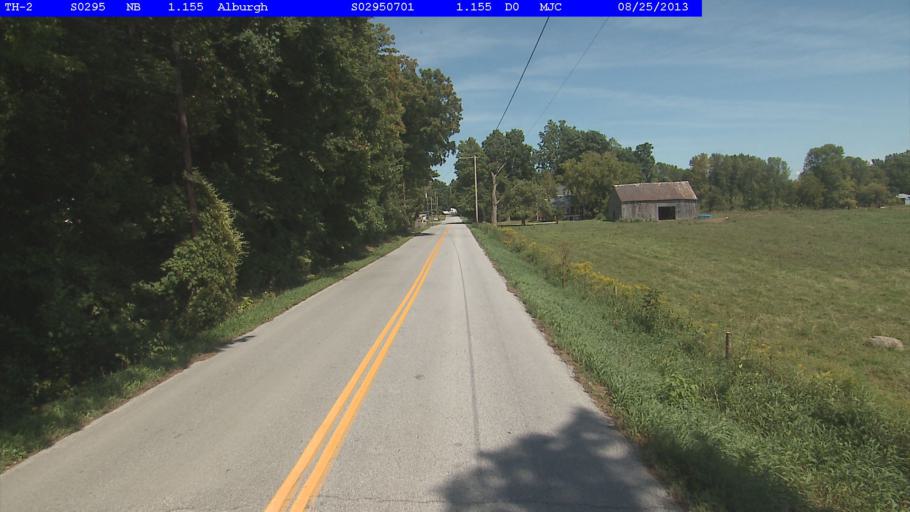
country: US
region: Vermont
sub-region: Franklin County
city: Swanton
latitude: 44.9902
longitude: -73.2238
